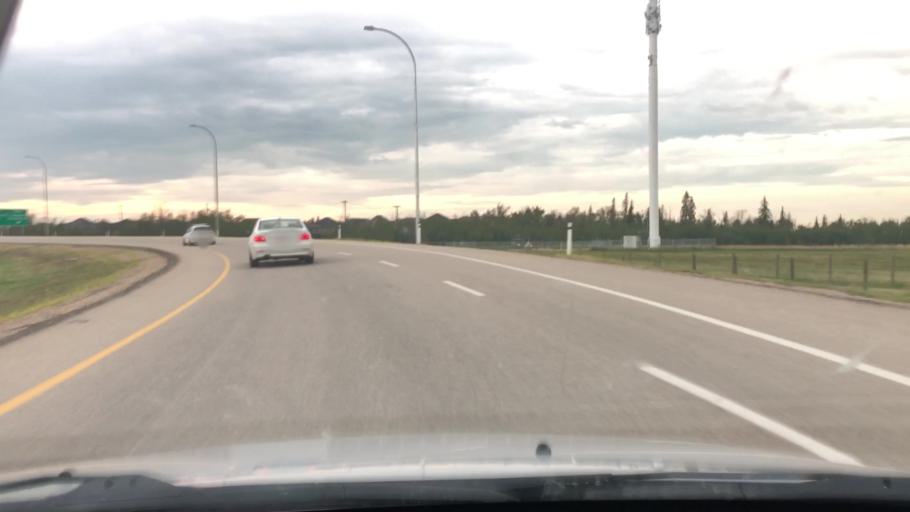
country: CA
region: Alberta
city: Devon
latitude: 53.4666
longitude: -113.6247
